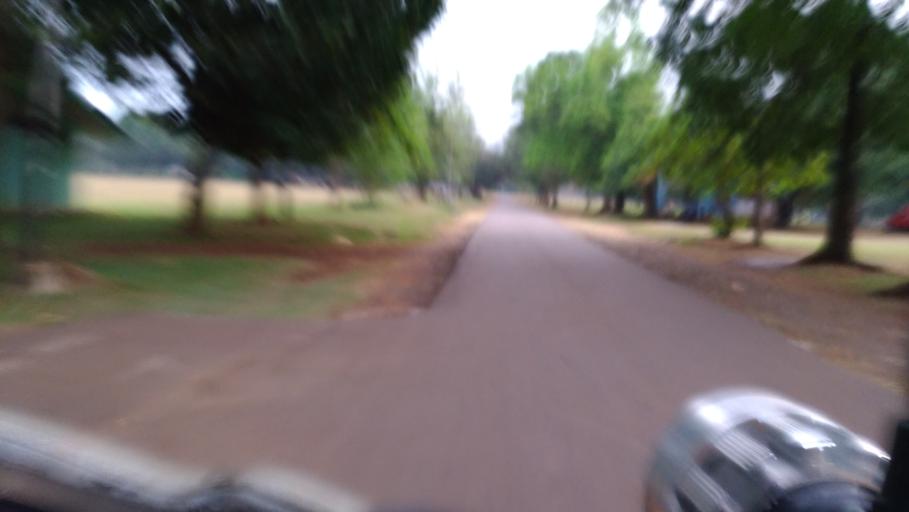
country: ID
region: West Java
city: Cileungsir
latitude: -6.3648
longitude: 106.9004
